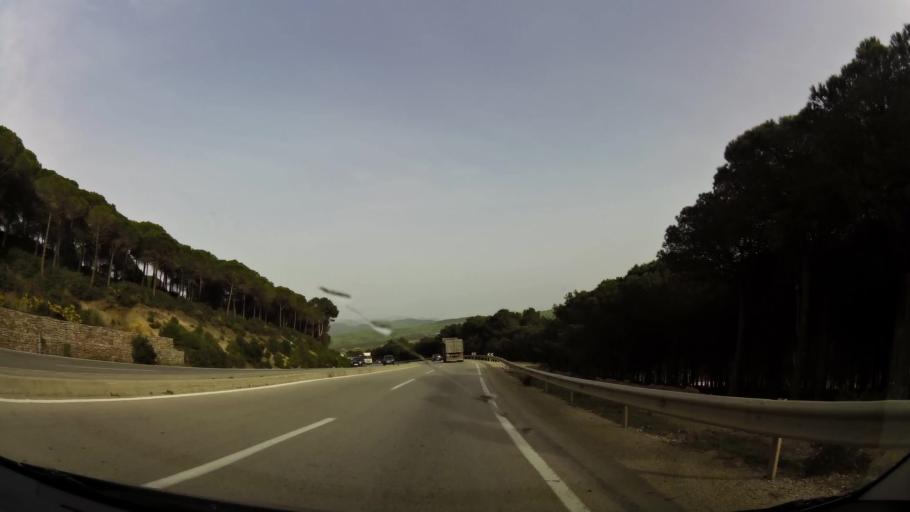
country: MA
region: Tanger-Tetouan
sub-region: Tetouan
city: Saddina
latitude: 35.5469
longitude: -5.5637
